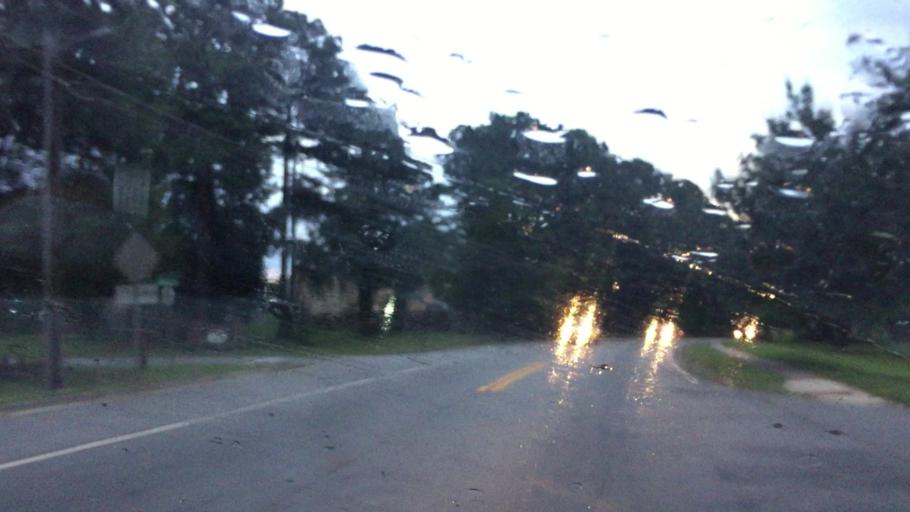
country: US
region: Georgia
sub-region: Clayton County
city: Riverdale
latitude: 33.5556
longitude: -84.3998
